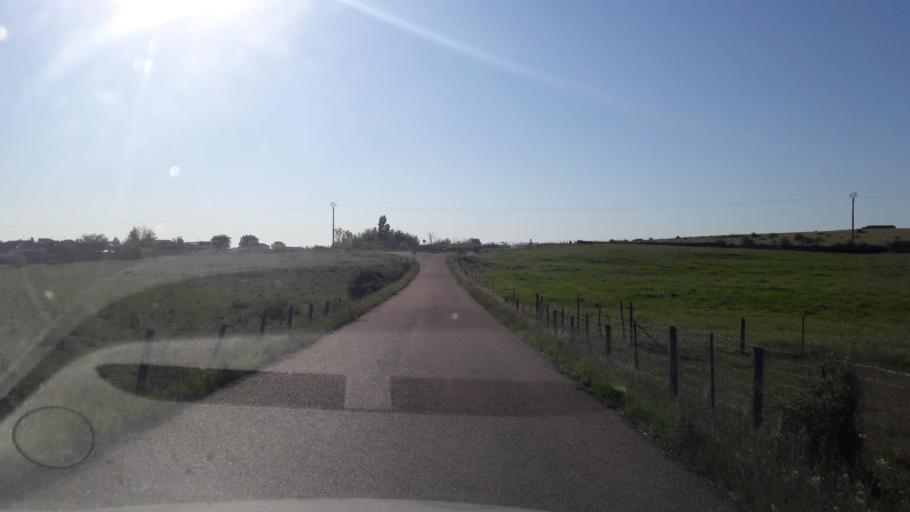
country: ES
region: Castille and Leon
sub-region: Provincia de Salamanca
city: Herguijuela del Campo
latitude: 40.6303
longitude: -5.8683
